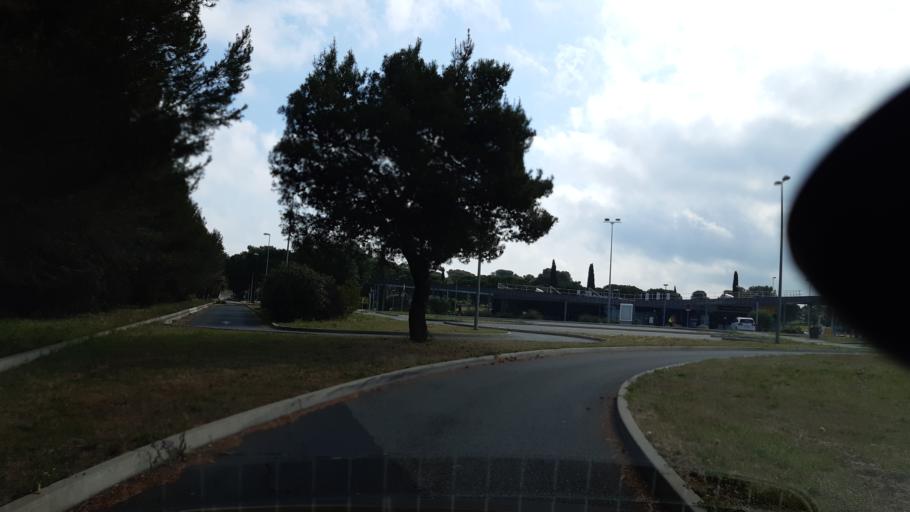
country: FR
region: Languedoc-Roussillon
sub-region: Departement de l'Herault
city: Montblanc
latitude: 43.3593
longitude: 3.3446
